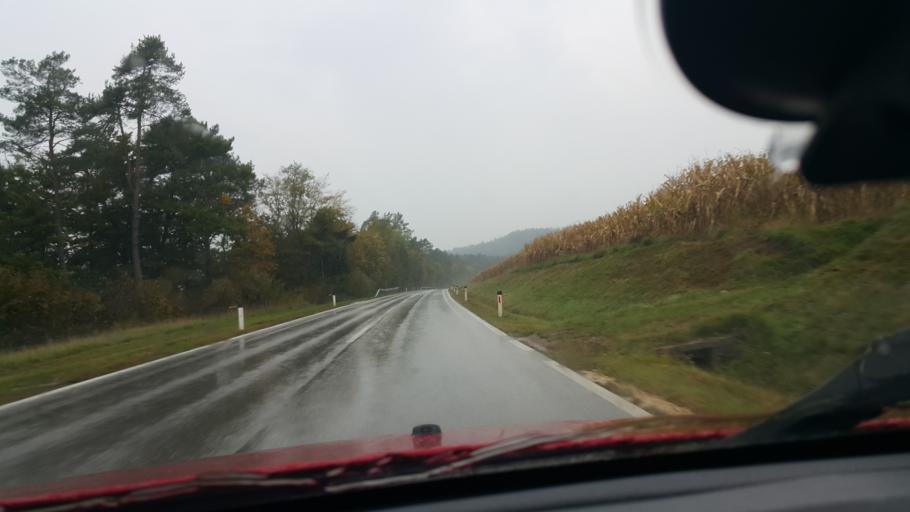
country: AT
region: Carinthia
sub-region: Politischer Bezirk Volkermarkt
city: Ruden
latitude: 46.6447
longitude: 14.8017
